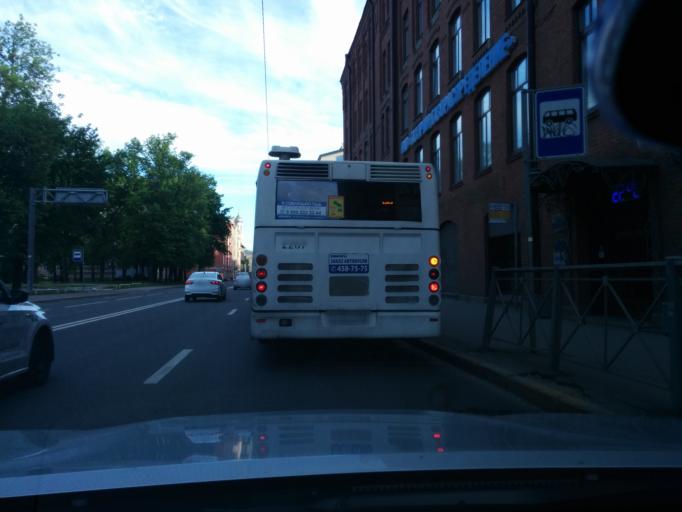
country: RU
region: Leningrad
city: Sampsonievskiy
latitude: 59.9746
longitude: 30.3391
